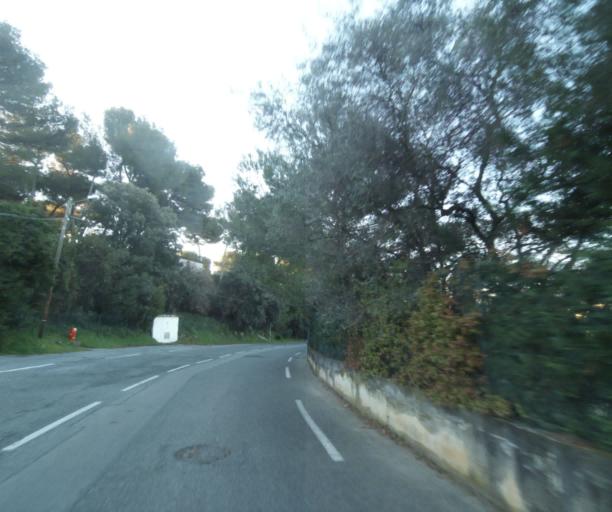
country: FR
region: Provence-Alpes-Cote d'Azur
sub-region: Departement des Alpes-Maritimes
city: Vallauris
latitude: 43.5843
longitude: 7.0815
